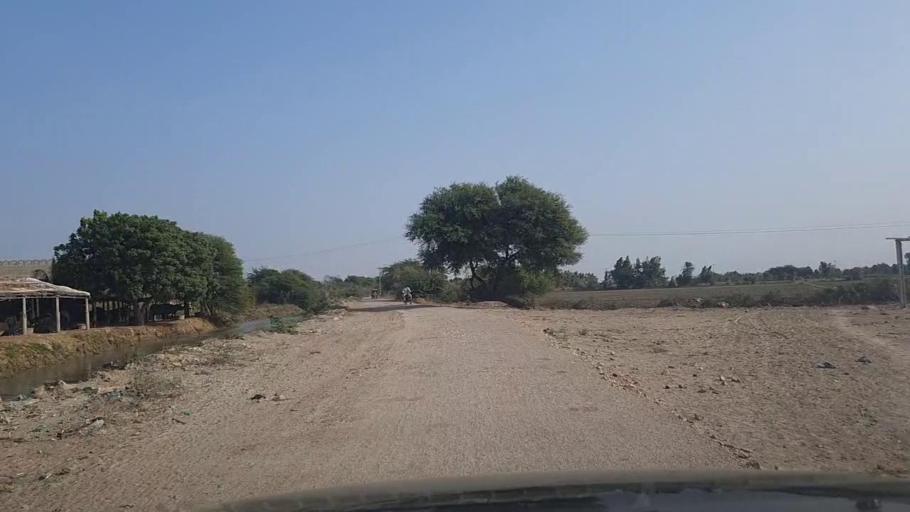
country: PK
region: Sindh
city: Mirpur Sakro
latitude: 24.6342
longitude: 67.7540
